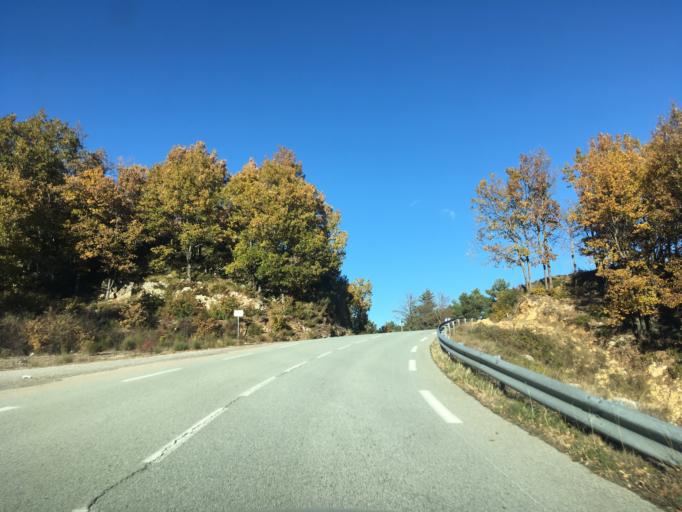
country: FR
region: Provence-Alpes-Cote d'Azur
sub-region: Departement du Var
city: Bargemon
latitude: 43.6829
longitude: 6.5106
